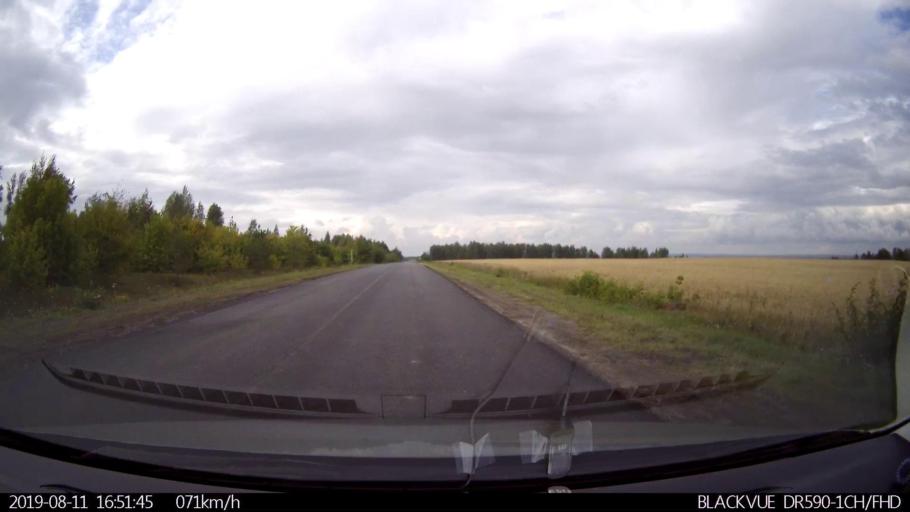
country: RU
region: Ulyanovsk
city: Mayna
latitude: 54.2403
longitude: 47.6761
